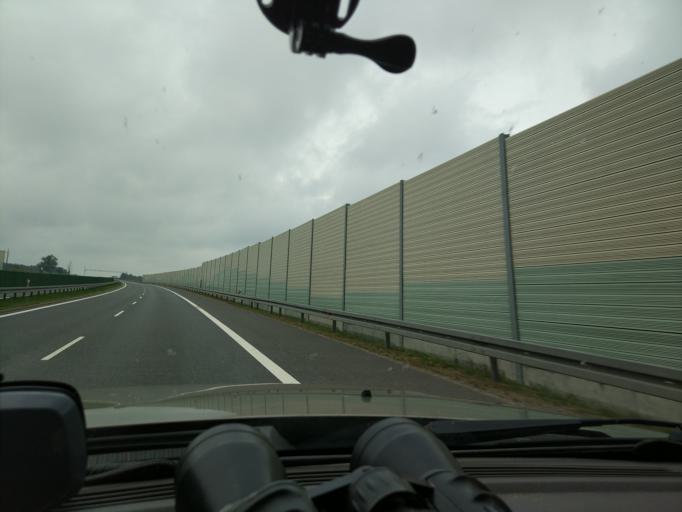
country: PL
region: Podlasie
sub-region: Powiat zambrowski
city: Zambrow
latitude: 53.0125
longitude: 22.3054
